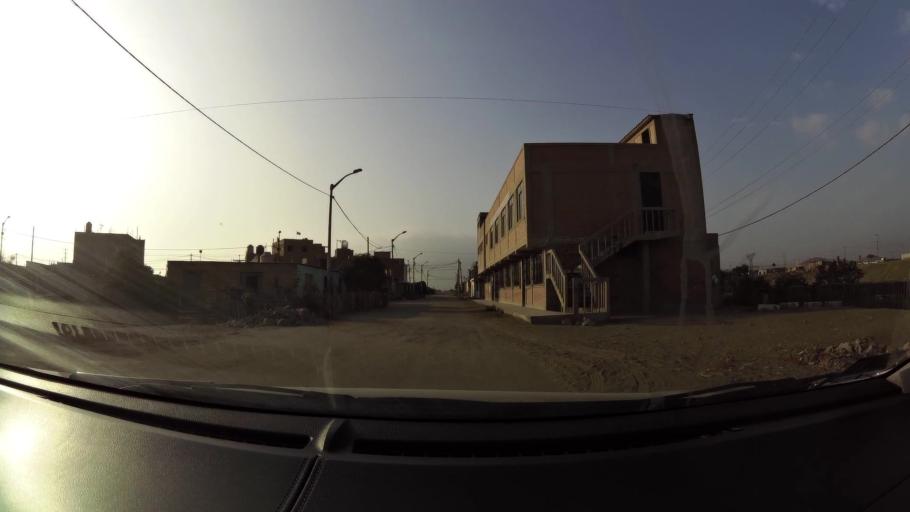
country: PE
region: Lima
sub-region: Lima
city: Santa Rosa
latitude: -11.7751
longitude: -77.1602
